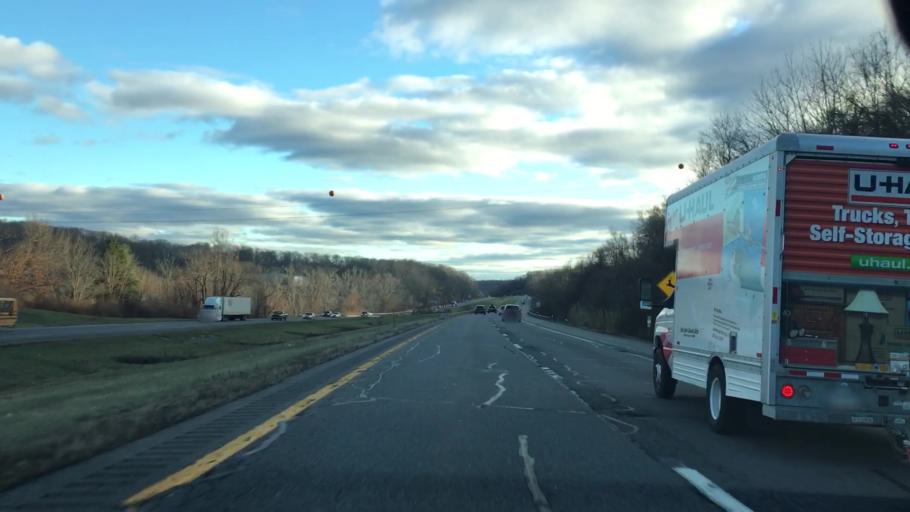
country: US
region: New York
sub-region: Putnam County
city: Lake Carmel
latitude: 41.4680
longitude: -73.6457
